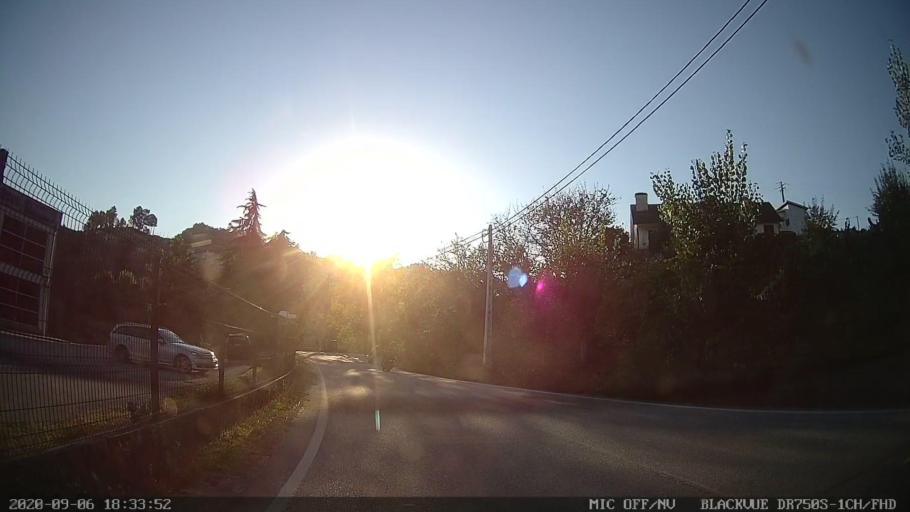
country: PT
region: Porto
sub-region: Amarante
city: Amarante
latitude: 41.2575
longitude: -8.0550
